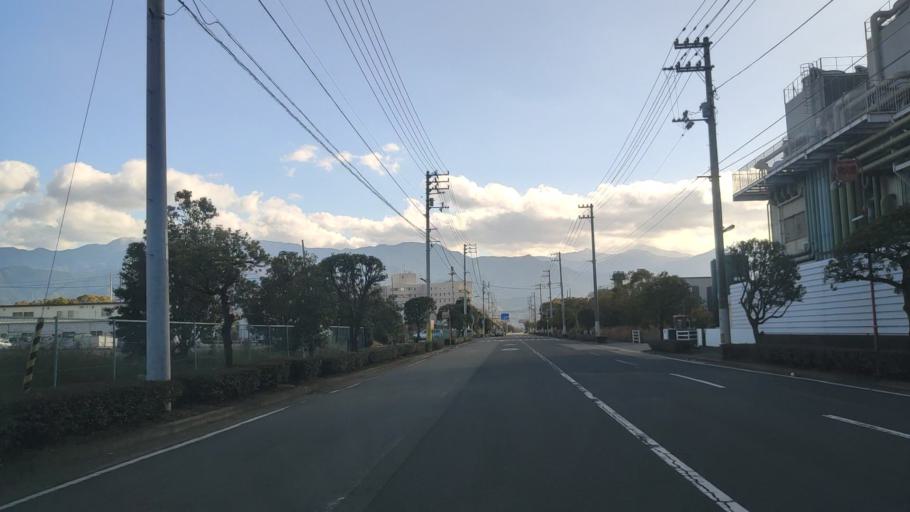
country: JP
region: Ehime
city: Saijo
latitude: 33.9381
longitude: 133.1918
